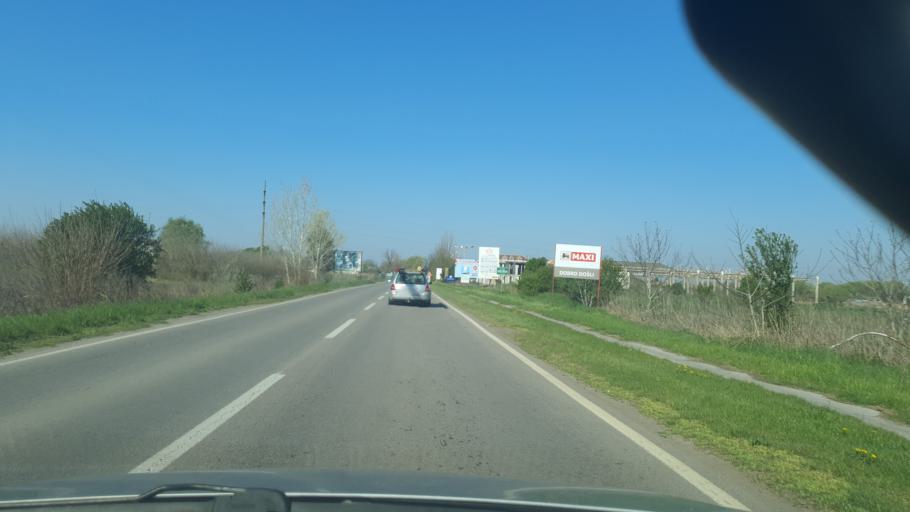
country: RS
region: Autonomna Pokrajina Vojvodina
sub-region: Zapadnobacki Okrug
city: Sombor
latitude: 45.7680
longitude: 19.1451
